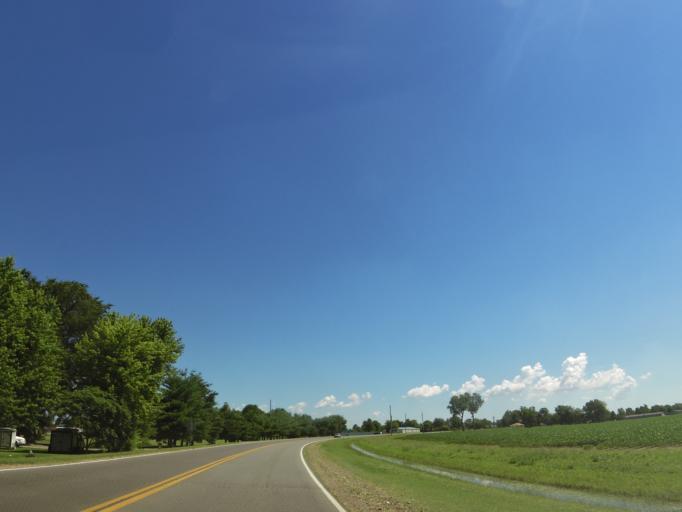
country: US
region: Missouri
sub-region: New Madrid County
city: Lilbourn
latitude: 36.5635
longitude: -89.6096
